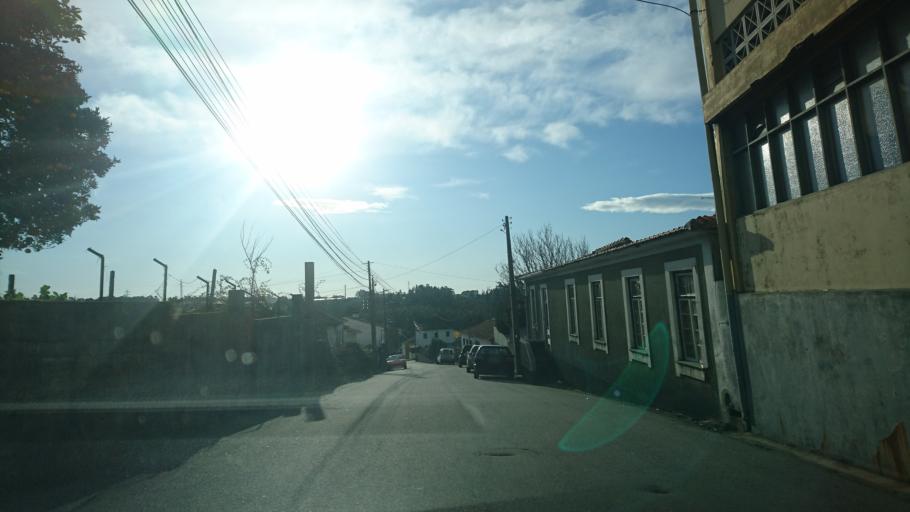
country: PT
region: Aveiro
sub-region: Santa Maria da Feira
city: Pacos de Brandao
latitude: 40.9680
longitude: -8.5933
